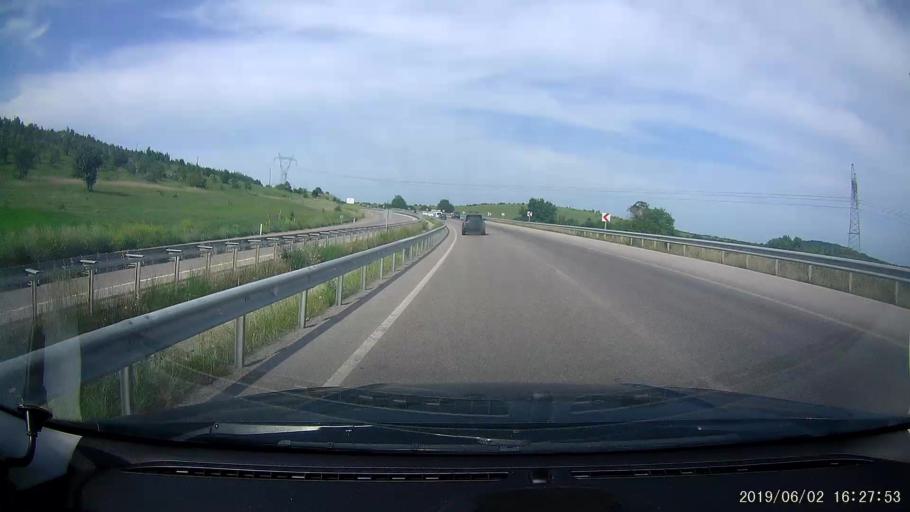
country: TR
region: Samsun
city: Ladik
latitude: 41.0030
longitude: 35.8372
